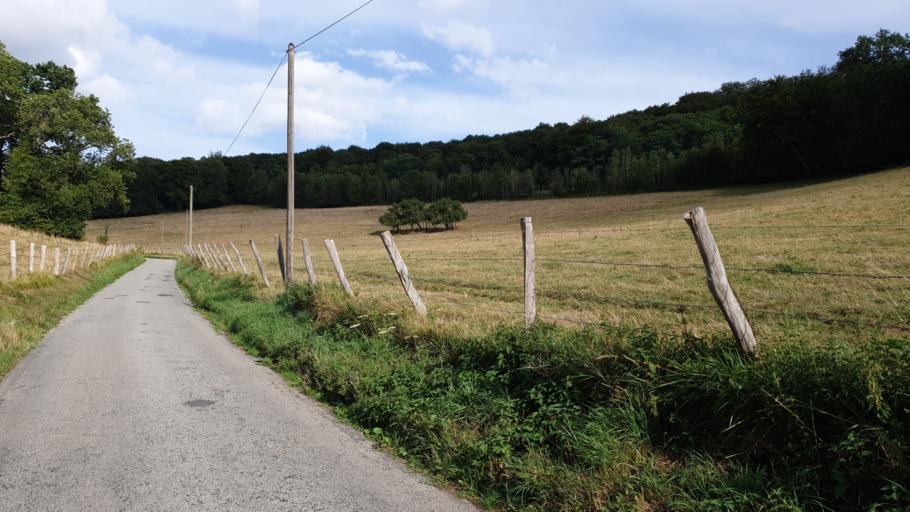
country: FR
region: Haute-Normandie
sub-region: Departement de la Seine-Maritime
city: Lillebonne
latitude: 49.5150
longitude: 0.5555
